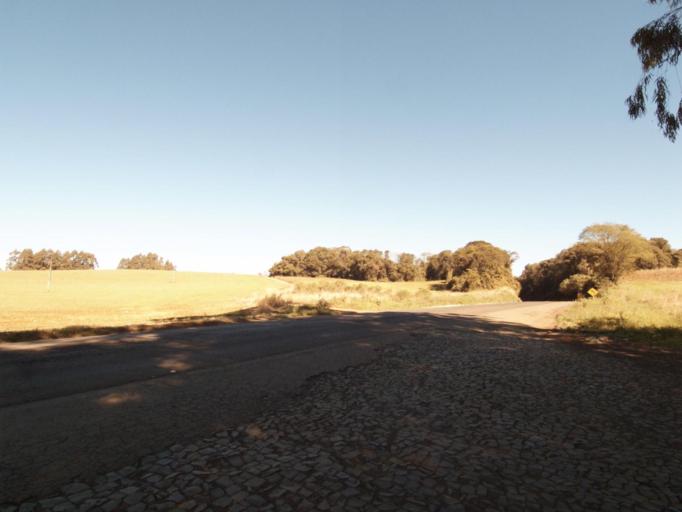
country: BR
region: Rio Grande do Sul
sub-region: Frederico Westphalen
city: Frederico Westphalen
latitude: -26.9187
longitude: -53.1955
